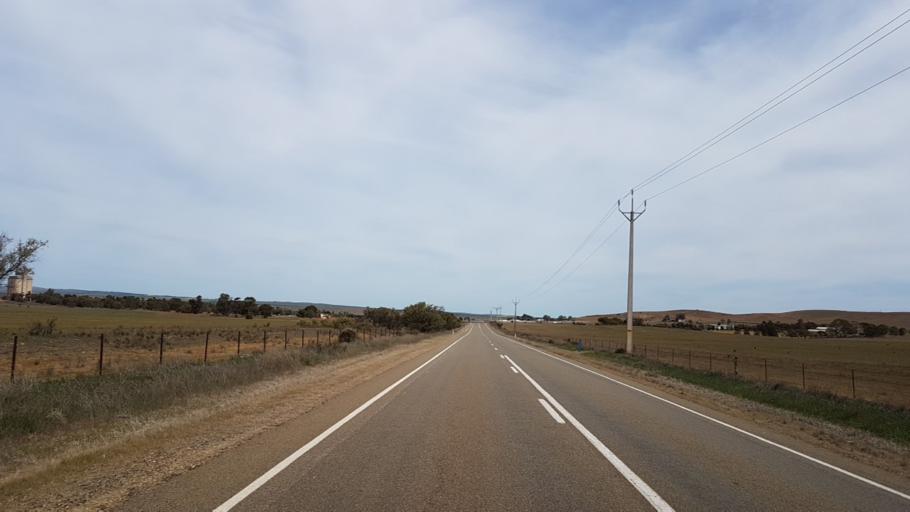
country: AU
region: South Australia
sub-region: Peterborough
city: Peterborough
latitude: -33.0187
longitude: 138.7549
